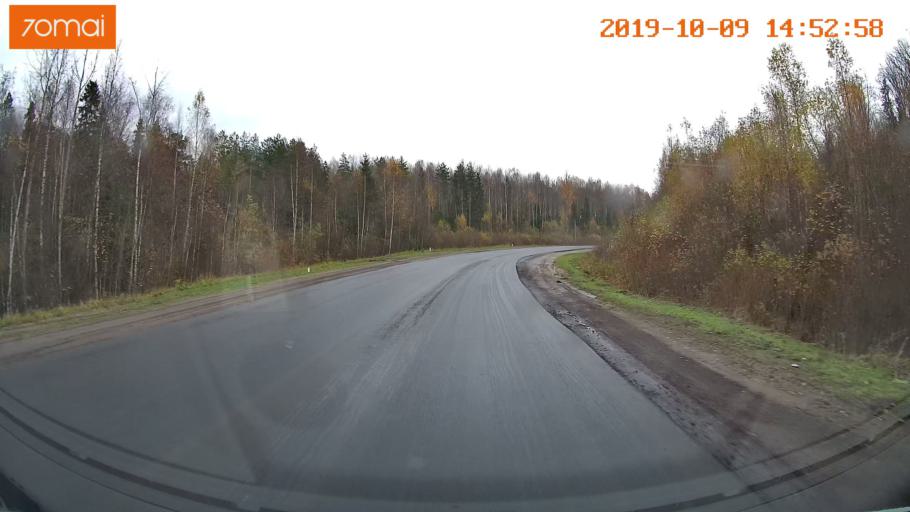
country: RU
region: Kostroma
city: Chistyye Bory
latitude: 58.3732
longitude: 41.6352
